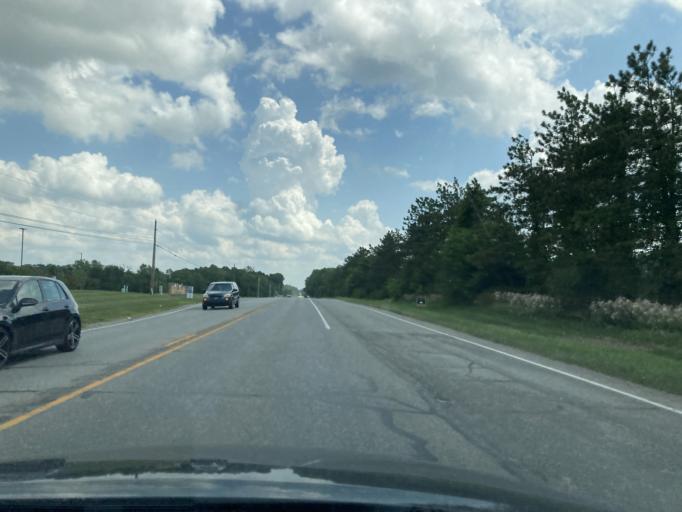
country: US
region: Indiana
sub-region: Boone County
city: Zionsville
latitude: 39.9871
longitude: -86.2592
